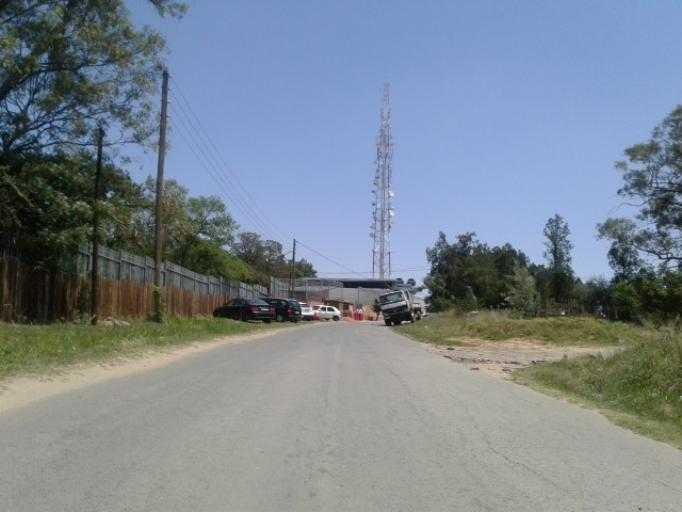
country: LS
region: Maseru
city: Maseru
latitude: -29.3070
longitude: 27.4779
